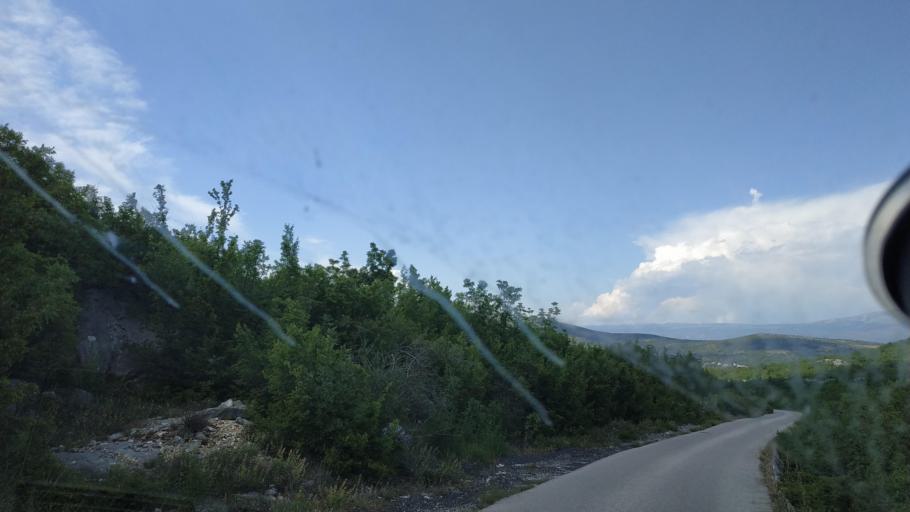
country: HR
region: Splitsko-Dalmatinska
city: Dugopolje
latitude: 43.5729
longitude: 16.6554
